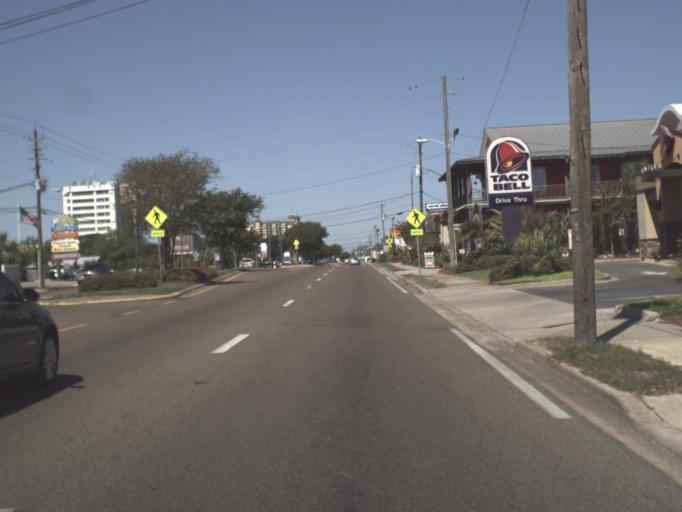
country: US
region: Florida
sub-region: Okaloosa County
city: Destin
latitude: 30.3928
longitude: -86.4985
